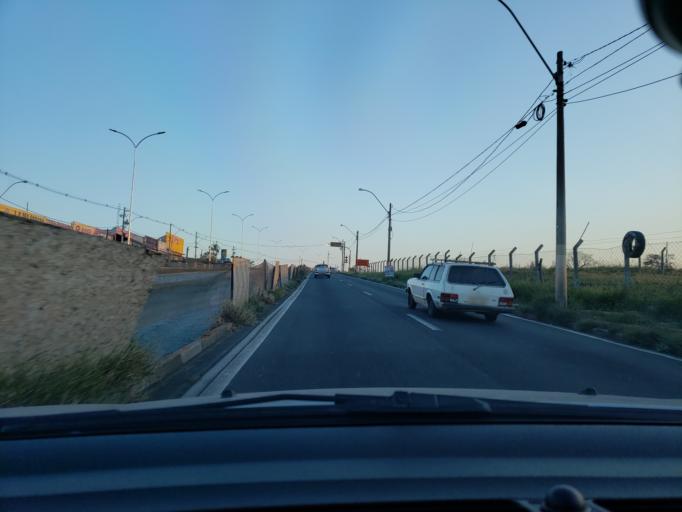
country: BR
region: Sao Paulo
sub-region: Campinas
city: Campinas
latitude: -22.9322
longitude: -47.1303
